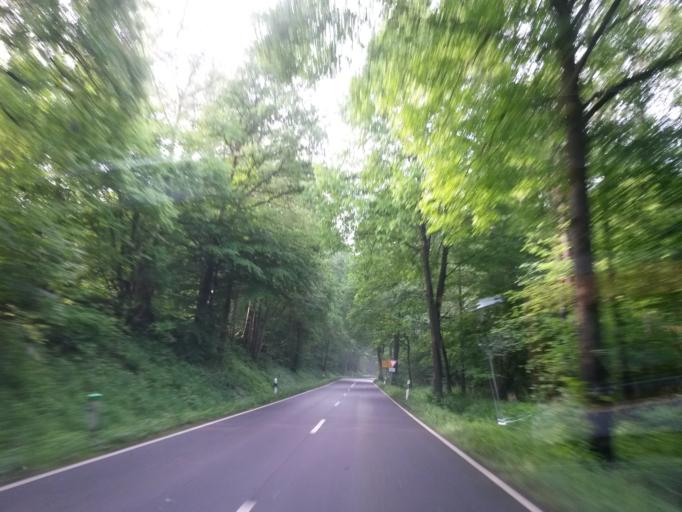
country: DE
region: North Rhine-Westphalia
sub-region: Regierungsbezirk Koln
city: Hennef
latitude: 50.8470
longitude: 7.3198
